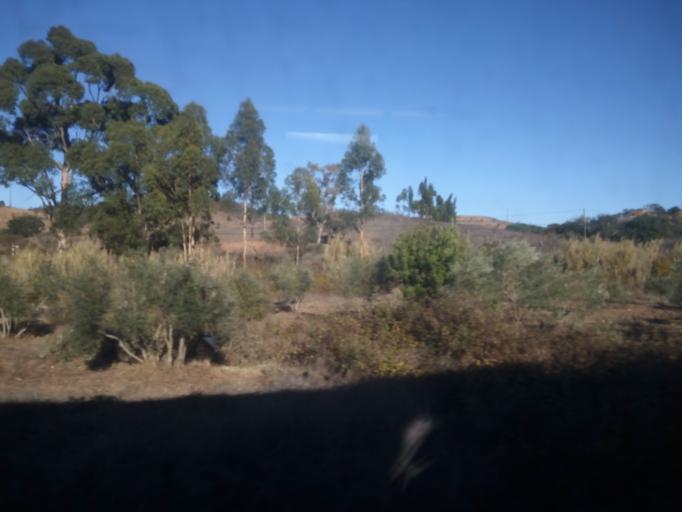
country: PT
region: Faro
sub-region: Silves
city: Sao Bartolomeu de Messines
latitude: 37.3278
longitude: -8.3383
